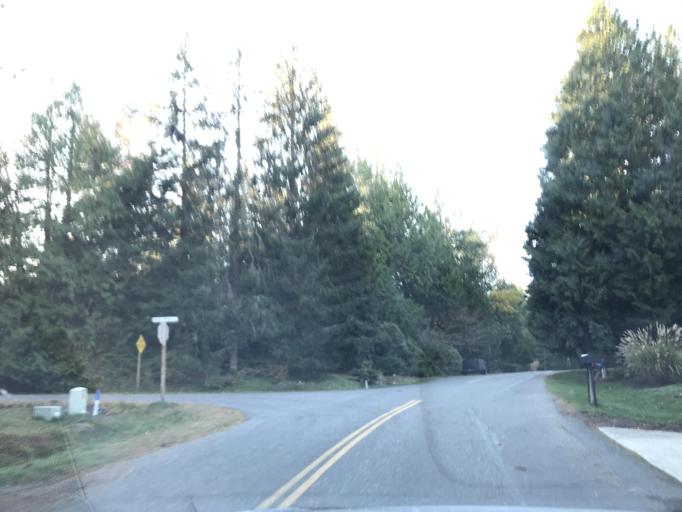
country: US
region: Washington
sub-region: Whatcom County
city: Geneva
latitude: 48.7415
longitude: -122.4127
